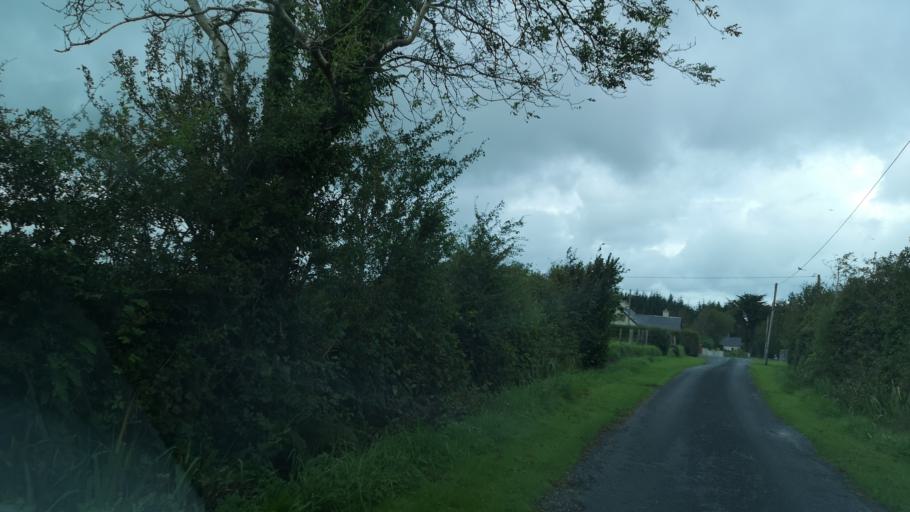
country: IE
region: Connaught
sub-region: County Galway
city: Athenry
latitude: 53.3054
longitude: -8.6985
